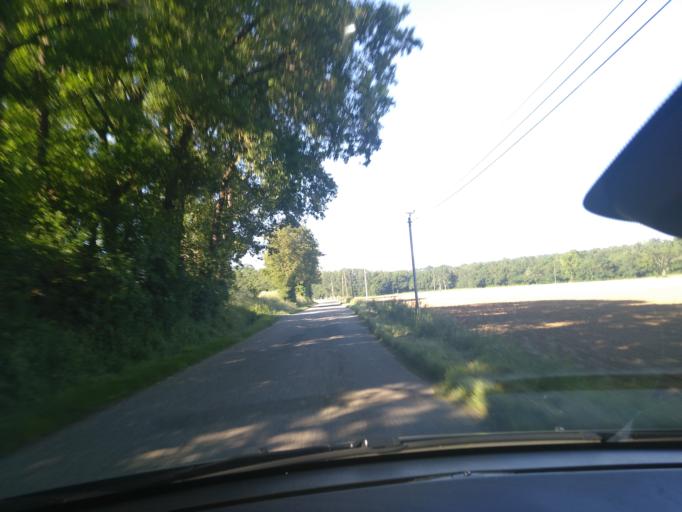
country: FR
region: Midi-Pyrenees
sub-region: Departement du Gers
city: Gimont
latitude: 43.7467
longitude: 0.9079
